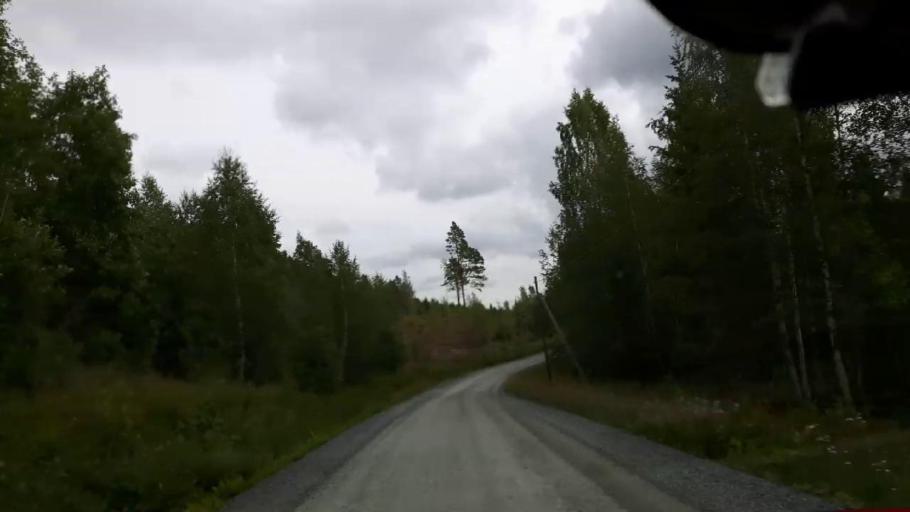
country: SE
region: Jaemtland
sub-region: Krokoms Kommun
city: Krokom
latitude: 63.5814
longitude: 14.1887
